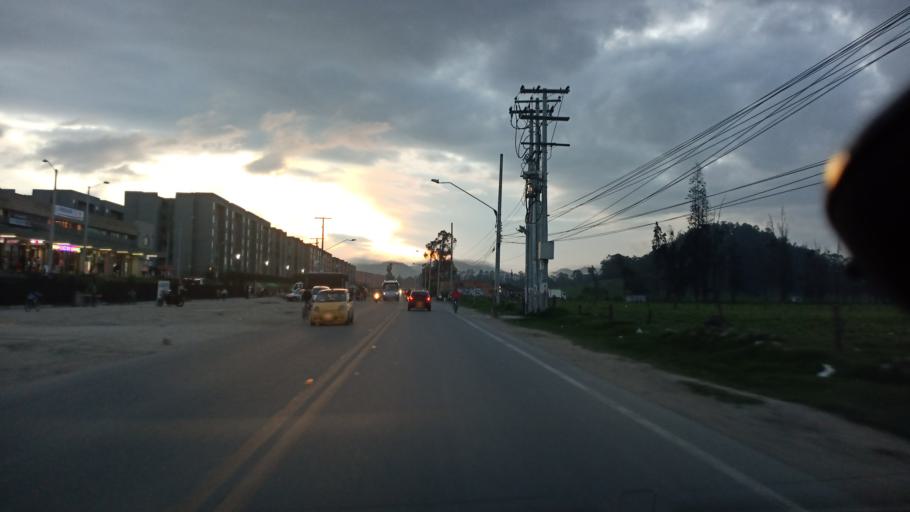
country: CO
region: Cundinamarca
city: Soacha
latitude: 4.5822
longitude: -74.2301
